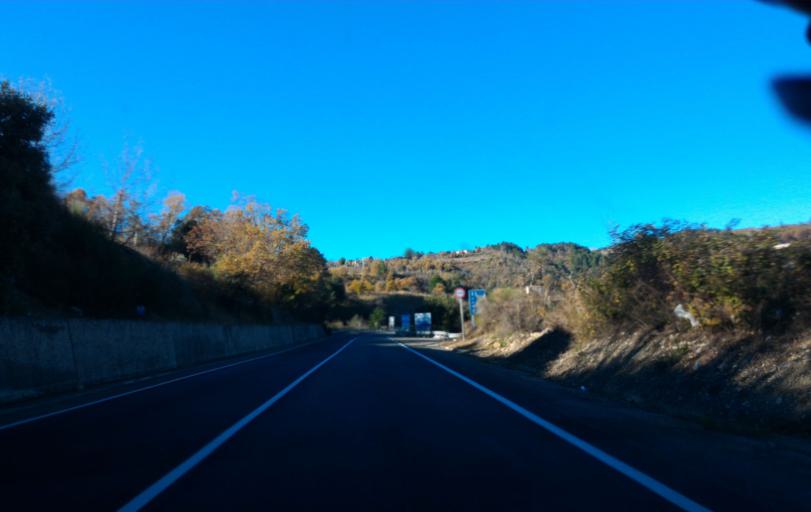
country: IT
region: Calabria
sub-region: Provincia di Crotone
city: Cerenzia
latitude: 39.2518
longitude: 16.7718
